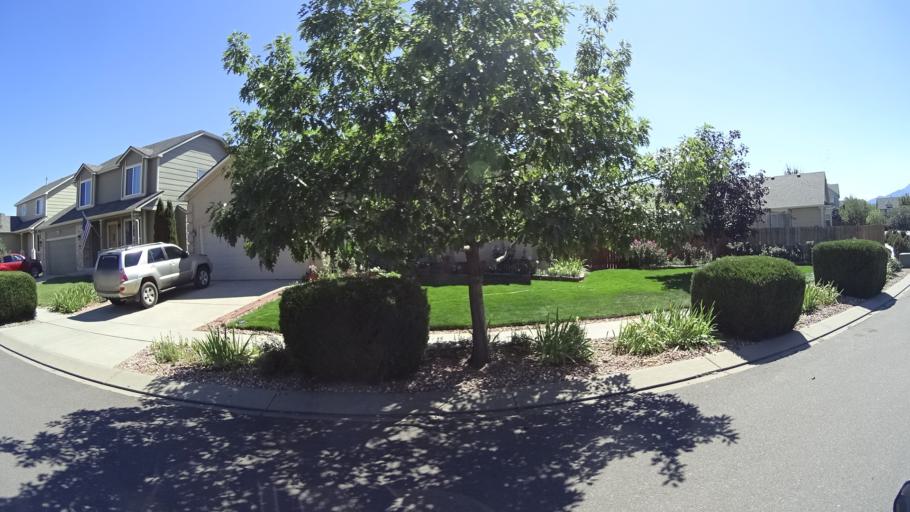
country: US
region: Colorado
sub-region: El Paso County
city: Security-Widefield
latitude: 38.7843
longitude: -104.7356
